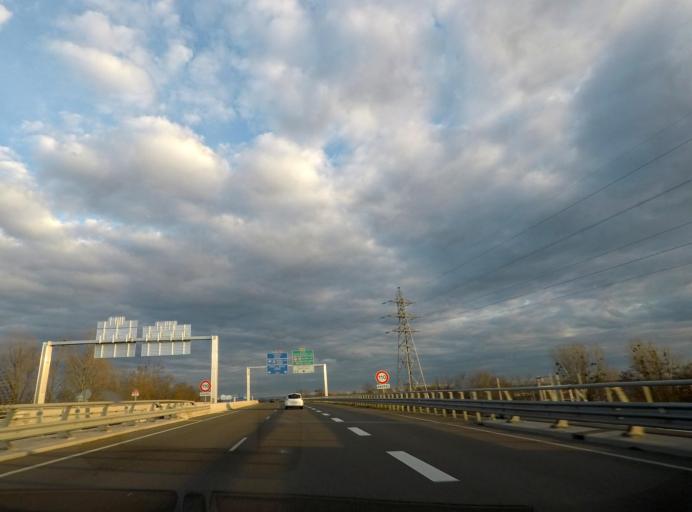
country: FR
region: Bourgogne
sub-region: Departement de Saone-et-Loire
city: Charnay-les-Macon
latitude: 46.2786
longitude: 4.7977
